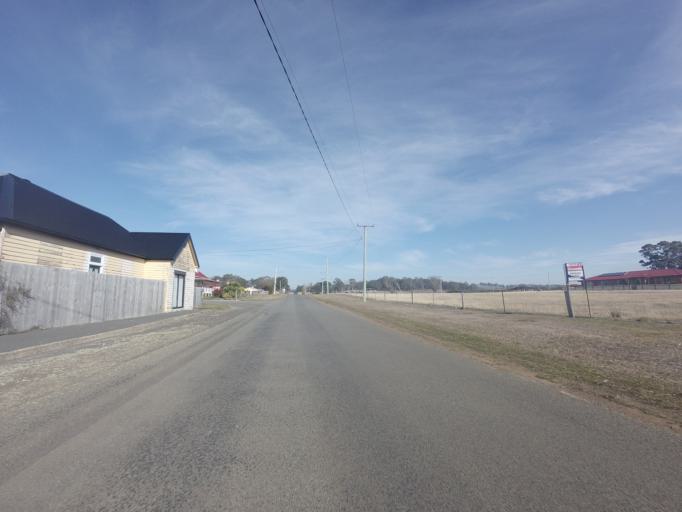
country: AU
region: Tasmania
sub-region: Sorell
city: Sorell
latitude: -42.4565
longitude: 147.4615
